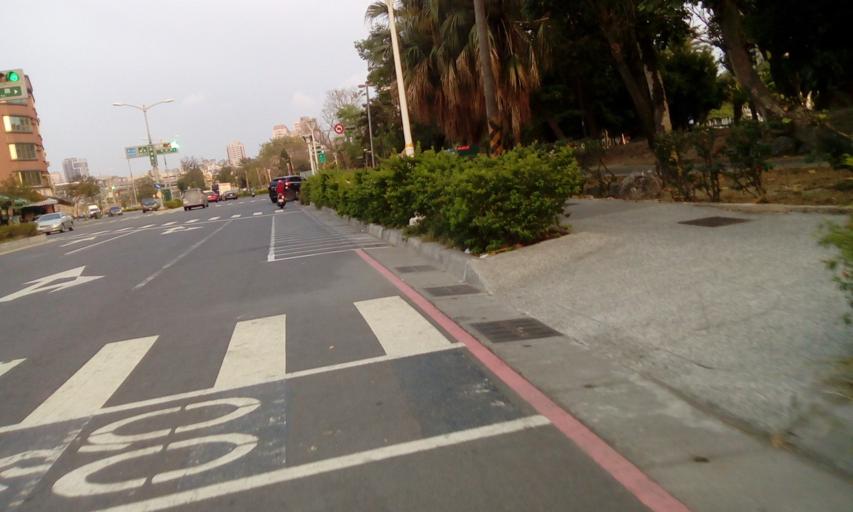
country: TW
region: Kaohsiung
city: Kaohsiung
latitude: 22.6896
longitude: 120.2998
